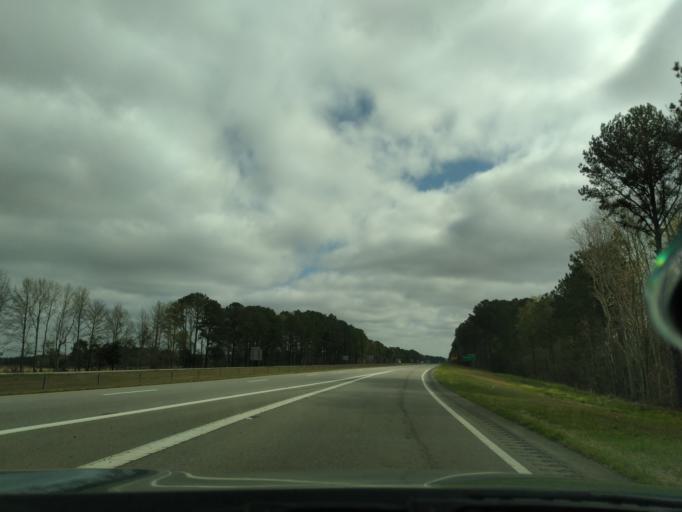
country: US
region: North Carolina
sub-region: Chowan County
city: Edenton
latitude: 36.0763
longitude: -76.6104
